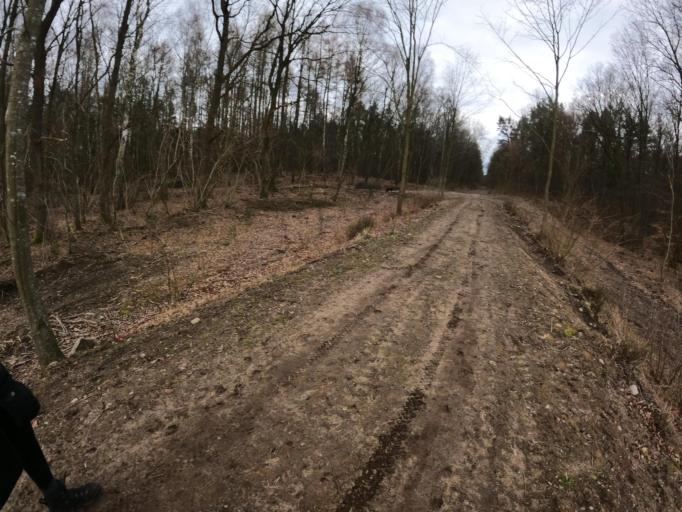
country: PL
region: West Pomeranian Voivodeship
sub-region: Powiat kamienski
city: Golczewo
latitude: 53.8162
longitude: 14.9916
